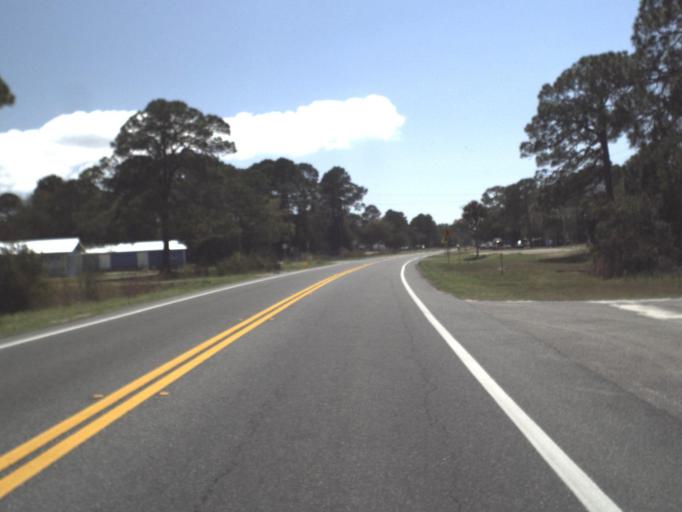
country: US
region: Florida
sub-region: Wakulla County
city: Crawfordville
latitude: 30.0226
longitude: -84.3906
